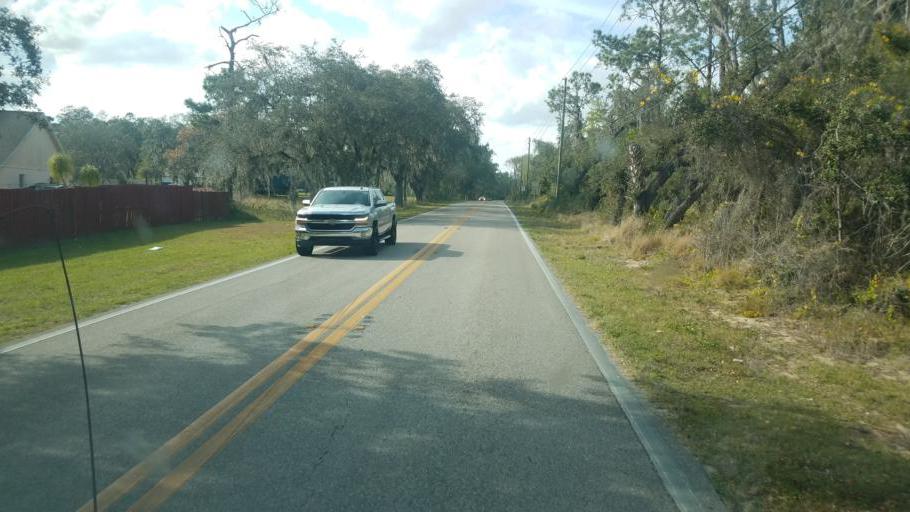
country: US
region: Florida
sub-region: Polk County
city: Loughman
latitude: 28.2540
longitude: -81.5742
